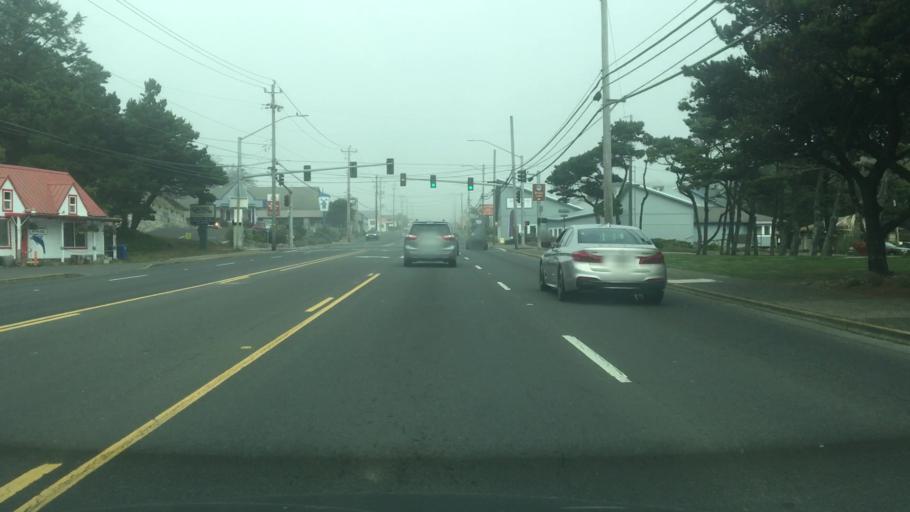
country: US
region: Oregon
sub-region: Lincoln County
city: Lincoln City
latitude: 44.9703
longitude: -124.0148
